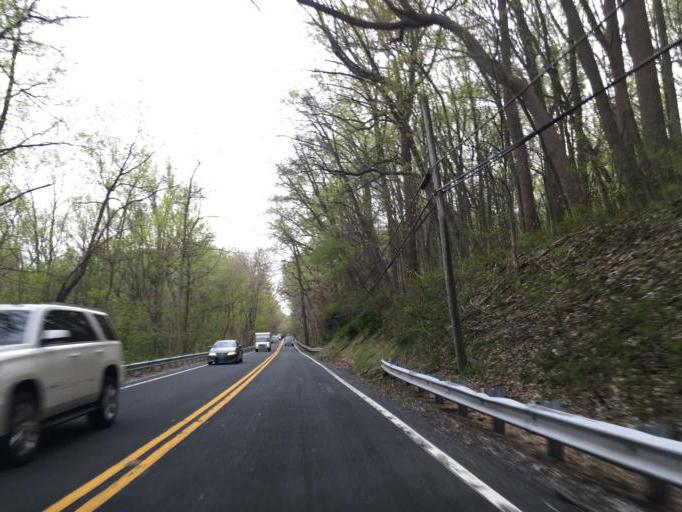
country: US
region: Maryland
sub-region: Baltimore County
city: Hampton
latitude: 39.4605
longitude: -76.5897
